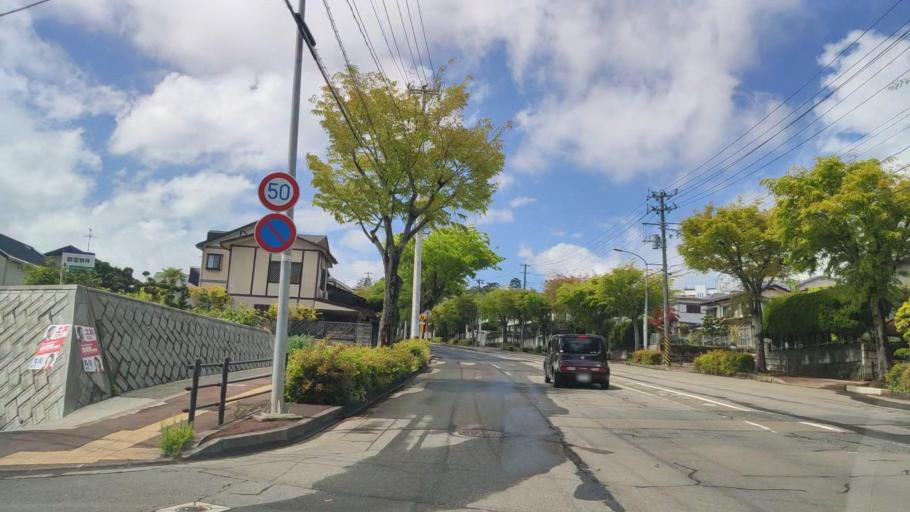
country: JP
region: Miyagi
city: Sendai
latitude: 38.2407
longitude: 140.8456
